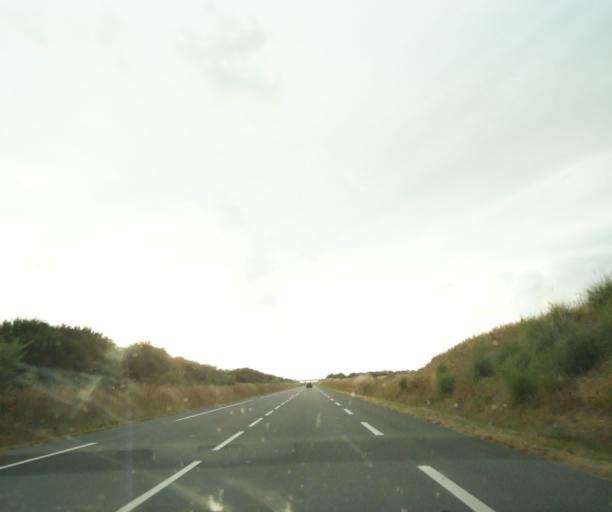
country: FR
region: Pays de la Loire
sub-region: Departement de la Vendee
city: Saint-Hilaire-de-Talmont
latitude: 46.4676
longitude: -1.6450
